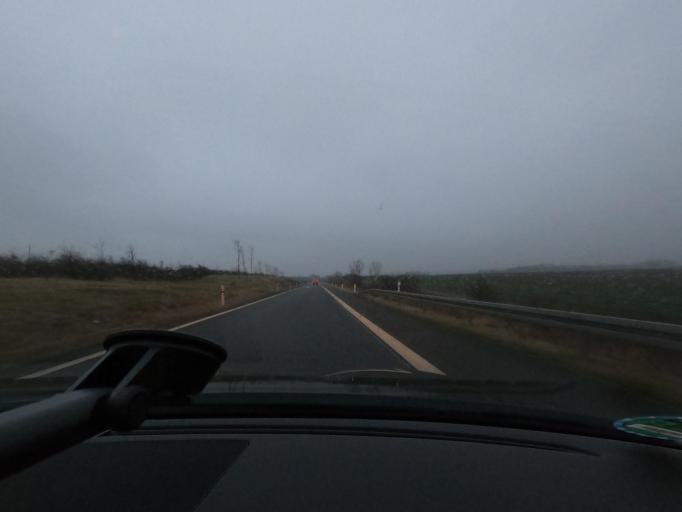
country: DE
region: Thuringia
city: Elxleben
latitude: 51.0264
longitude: 10.9727
